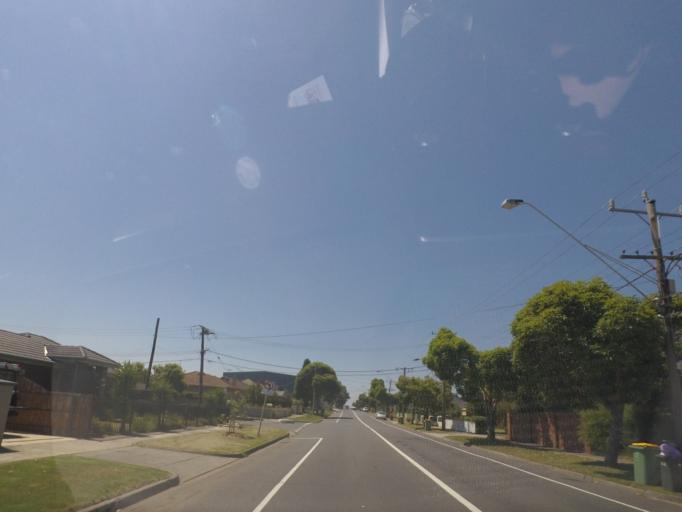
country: AU
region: Victoria
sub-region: Darebin
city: Reservoir
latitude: -37.7122
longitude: 144.9895
